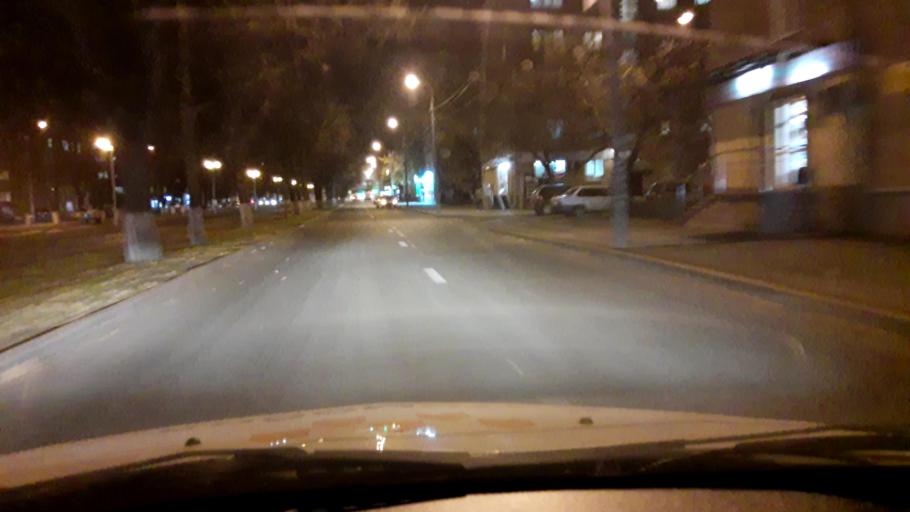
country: RU
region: Bashkortostan
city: Ufa
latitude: 54.7906
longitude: 56.0313
